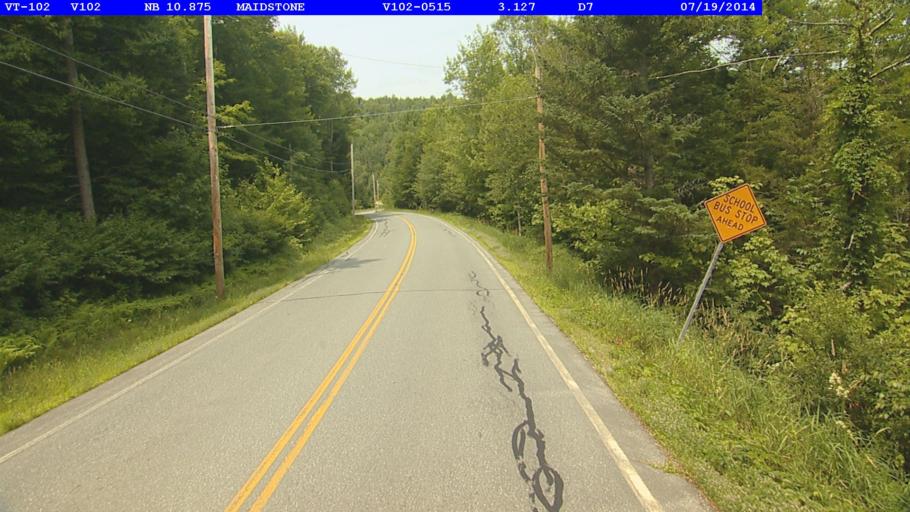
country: US
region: Vermont
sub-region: Essex County
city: Guildhall
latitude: 44.6073
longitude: -71.5606
